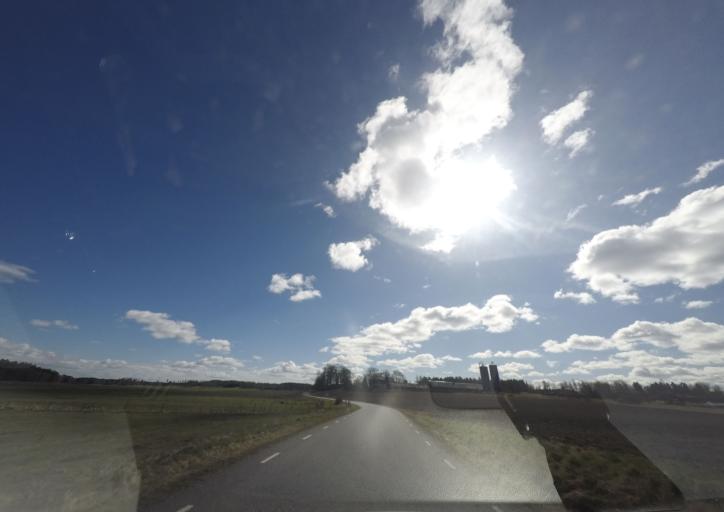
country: SE
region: OEstergoetland
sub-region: Norrkopings Kommun
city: Krokek
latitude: 58.8218
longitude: 16.4527
